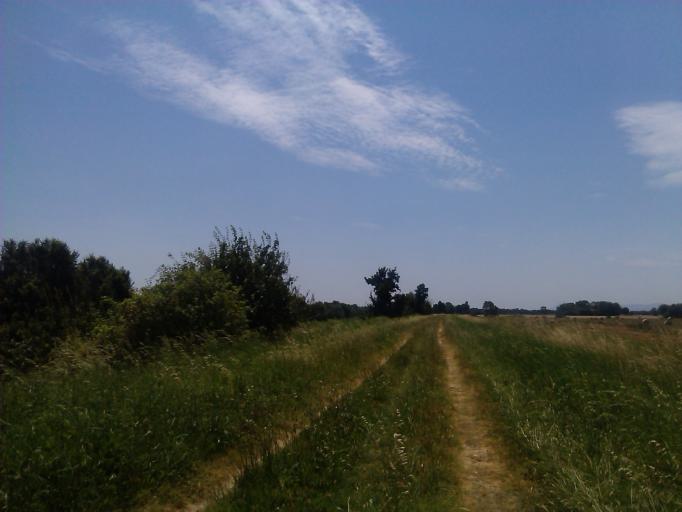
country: IT
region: Tuscany
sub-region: Province of Arezzo
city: Cesa
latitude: 43.3282
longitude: 11.8321
